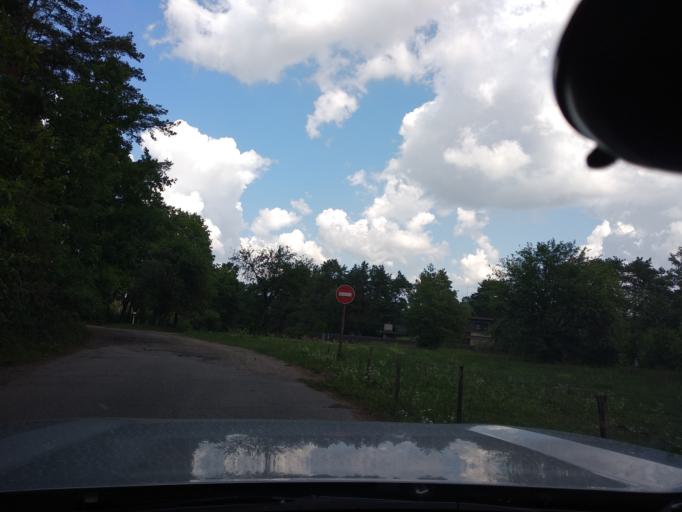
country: LT
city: Grigiskes
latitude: 54.6817
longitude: 25.0789
